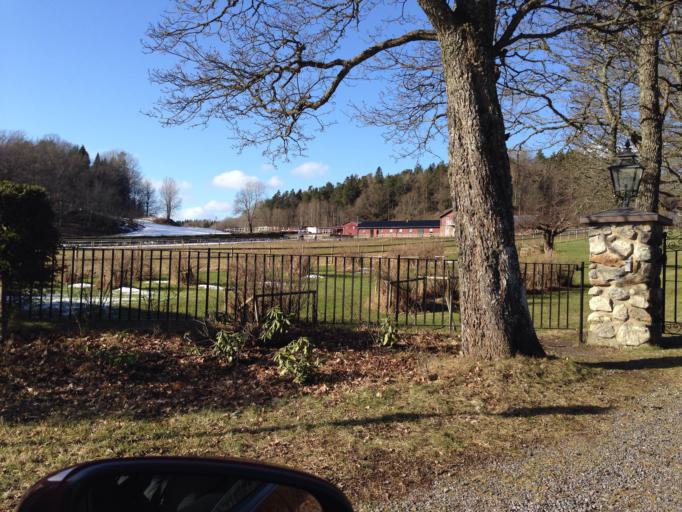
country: SE
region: Stockholm
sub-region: Botkyrka Kommun
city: Varsta
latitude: 59.1364
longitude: 17.7763
